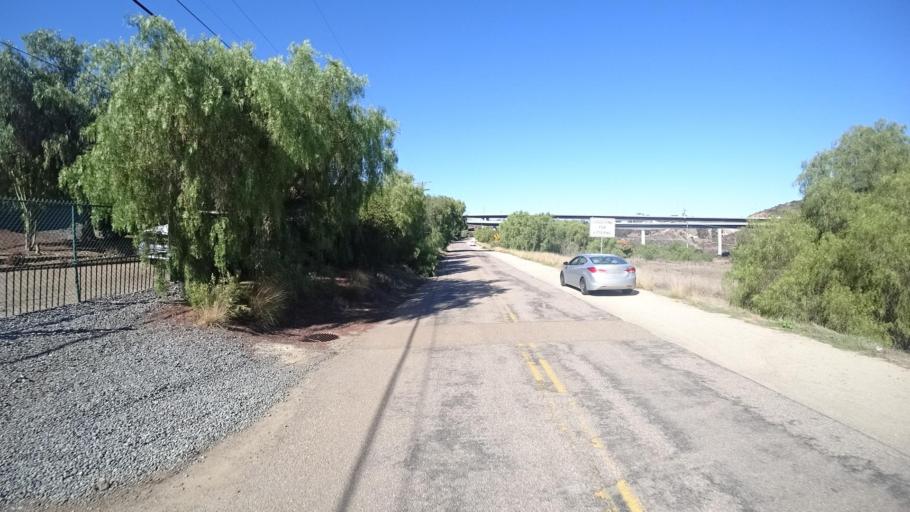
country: US
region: California
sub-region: San Diego County
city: La Presa
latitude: 32.6868
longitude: -117.0155
